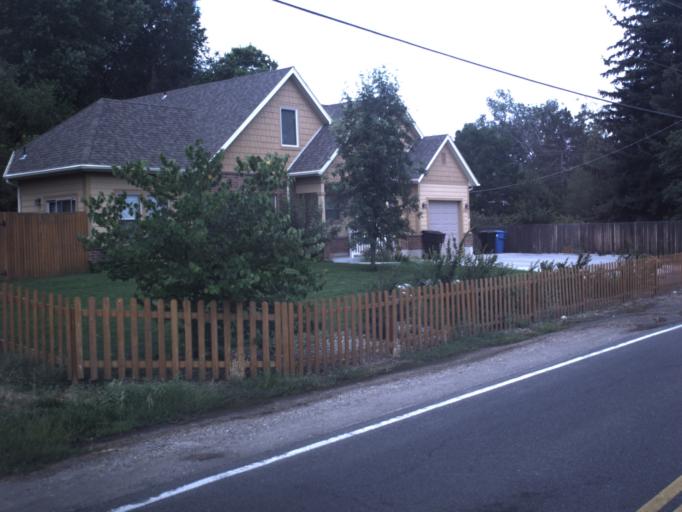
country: US
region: Utah
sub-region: Weber County
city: Riverdale
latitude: 41.1646
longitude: -112.0064
